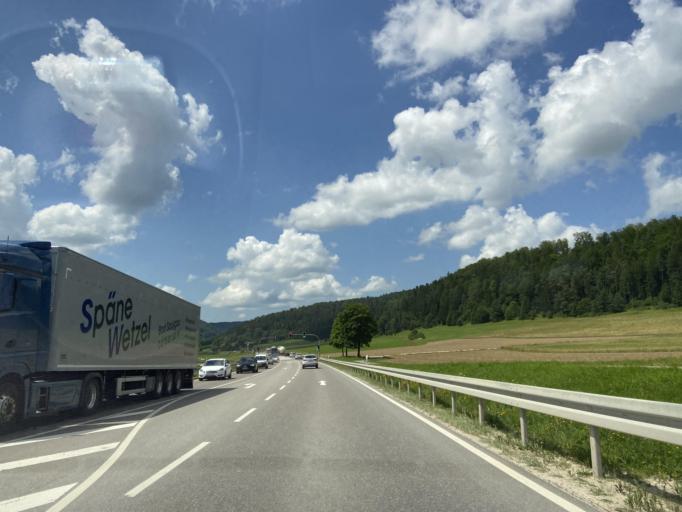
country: DE
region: Baden-Wuerttemberg
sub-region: Tuebingen Region
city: Strassberg
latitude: 48.1925
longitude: 9.0876
